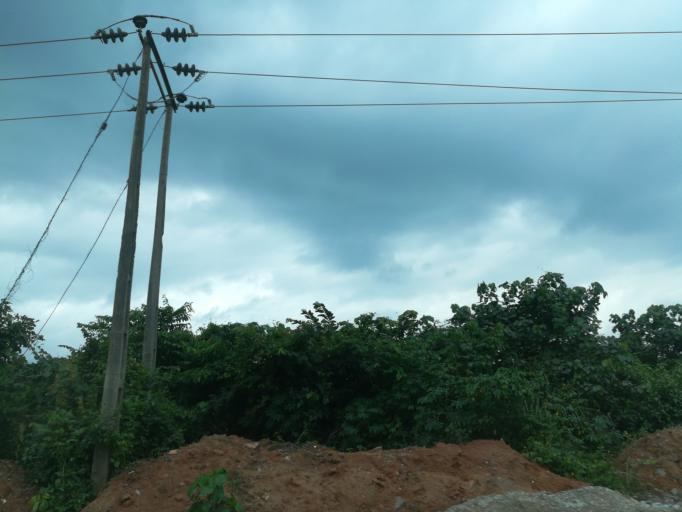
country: NG
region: Lagos
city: Ejirin
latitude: 6.6460
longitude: 3.8431
